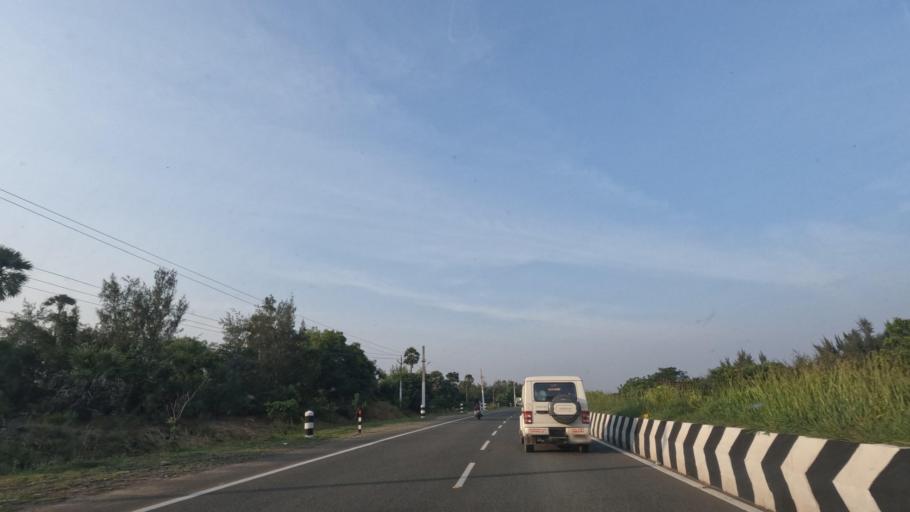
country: IN
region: Tamil Nadu
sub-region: Kancheepuram
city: Mamallapuram
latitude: 12.6675
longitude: 80.2099
